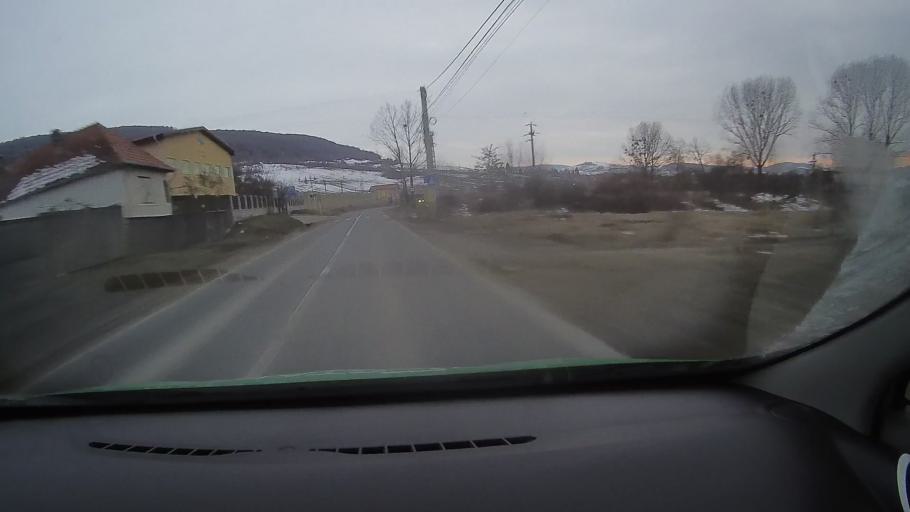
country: RO
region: Harghita
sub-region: Municipiul Odorheiu Secuiesc
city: Odorheiu Secuiesc
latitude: 46.2834
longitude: 25.2897
